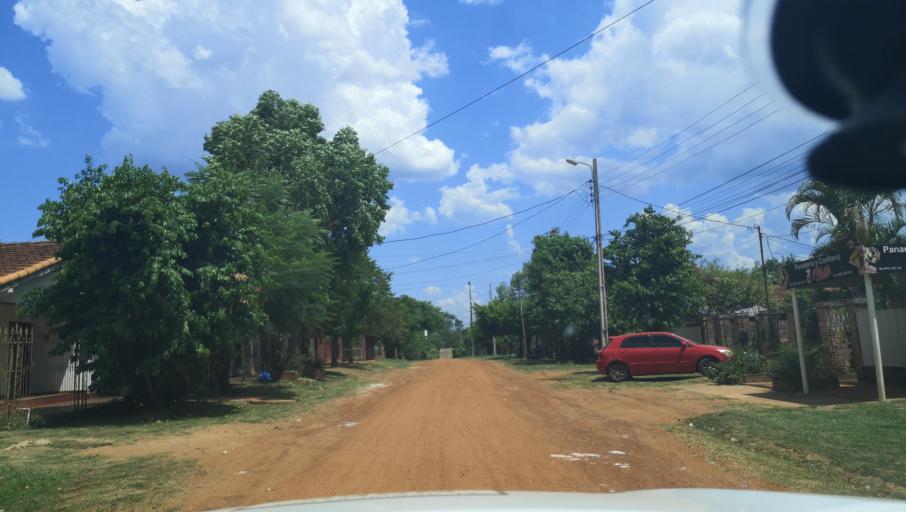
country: PY
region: Itapua
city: Carmen del Parana
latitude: -27.1684
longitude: -56.2452
